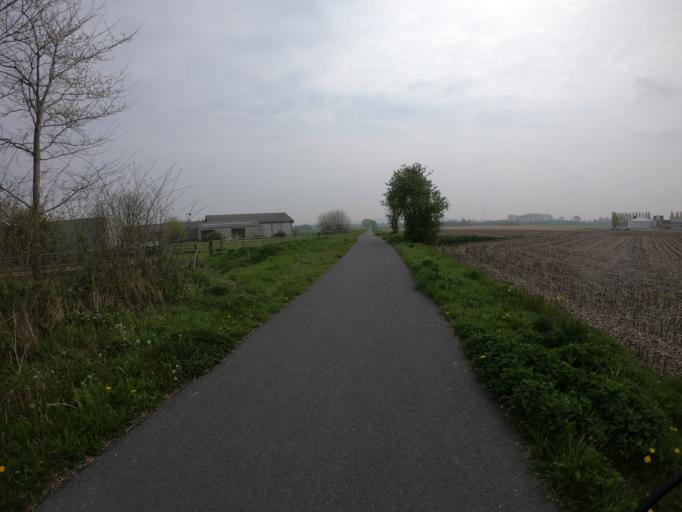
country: BE
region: Flanders
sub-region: Provincie West-Vlaanderen
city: Avelgem
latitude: 50.7766
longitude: 3.4122
